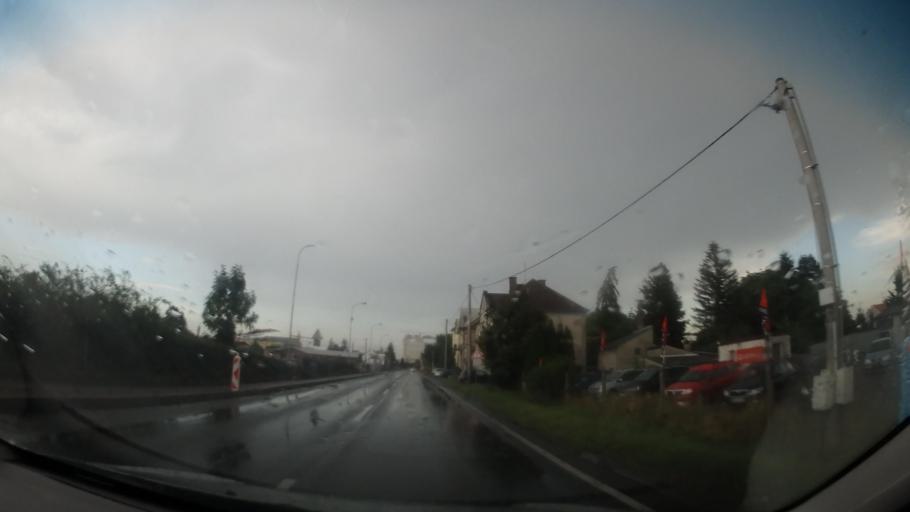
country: CZ
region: Olomoucky
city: Litovel
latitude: 49.6913
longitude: 17.0697
